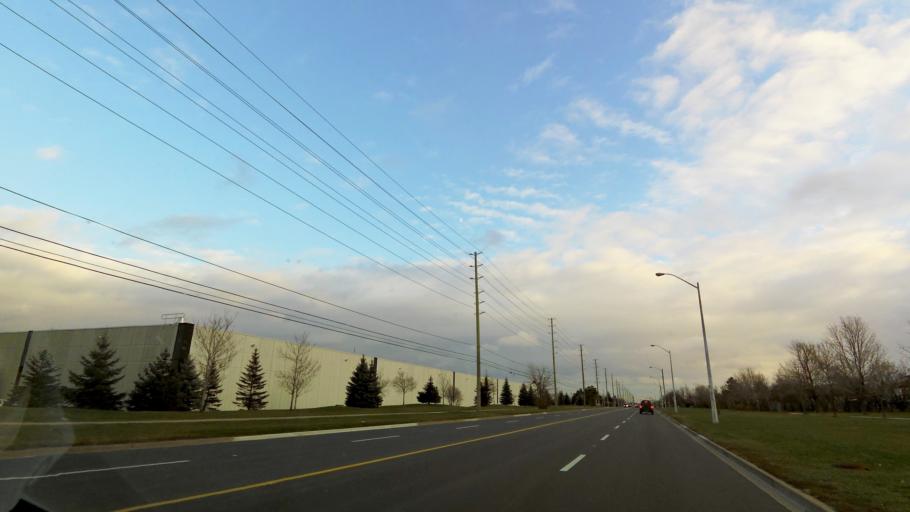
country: CA
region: Ontario
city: Brampton
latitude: 43.7402
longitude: -79.7157
